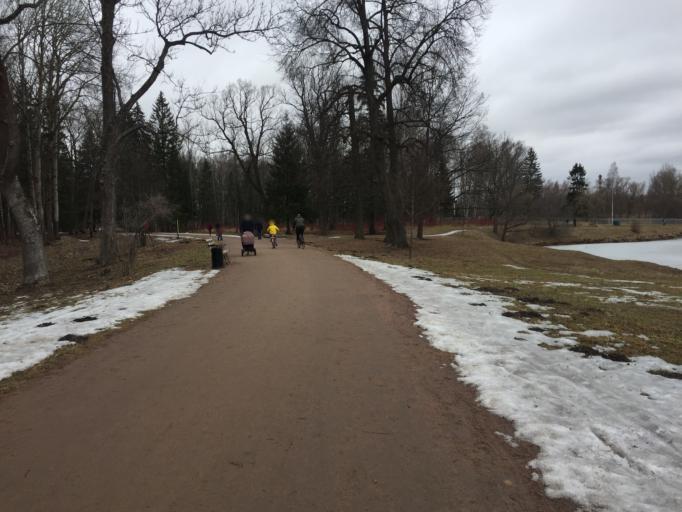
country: RU
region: St.-Petersburg
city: Pushkin
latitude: 59.7245
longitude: 30.3675
